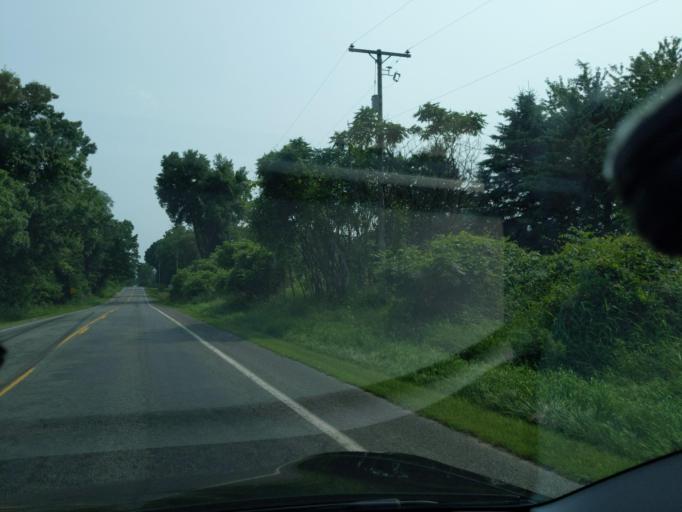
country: US
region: Michigan
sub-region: Eaton County
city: Eaton Rapids
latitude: 42.4807
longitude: -84.5609
